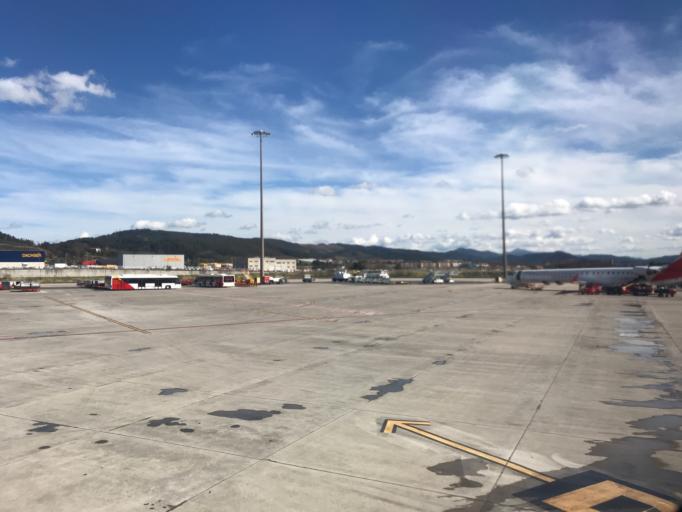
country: ES
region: Basque Country
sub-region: Bizkaia
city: Sondika
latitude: 43.3029
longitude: -2.9056
